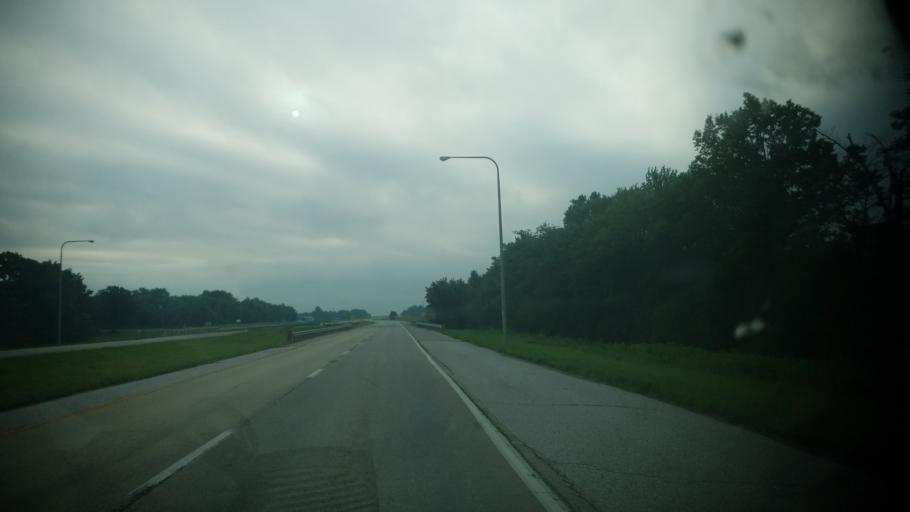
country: US
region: Illinois
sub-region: Clay County
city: Flora
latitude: 38.6744
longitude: -88.4376
